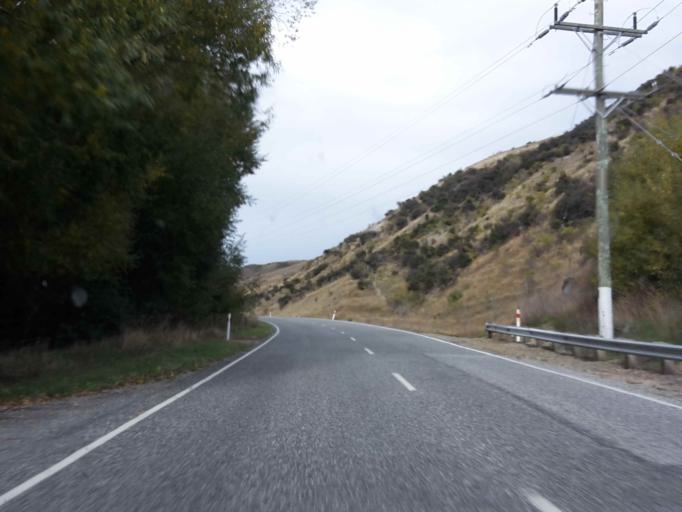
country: NZ
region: Otago
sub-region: Queenstown-Lakes District
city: Wanaka
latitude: -44.7882
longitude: 169.0806
